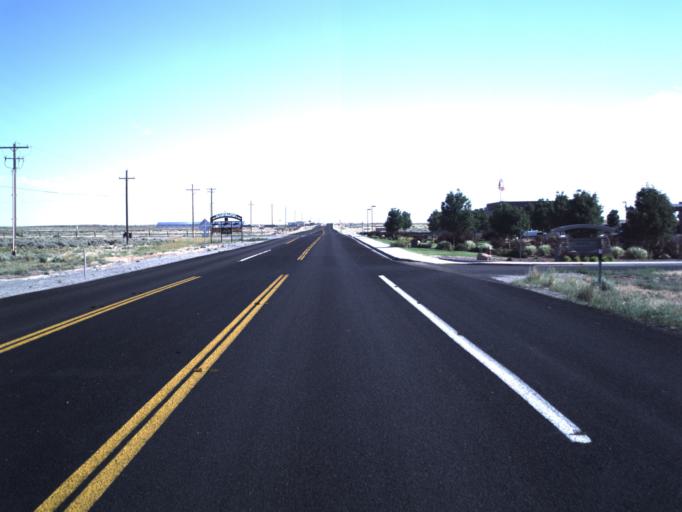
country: US
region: Utah
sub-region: Beaver County
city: Milford
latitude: 38.4060
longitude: -113.0098
